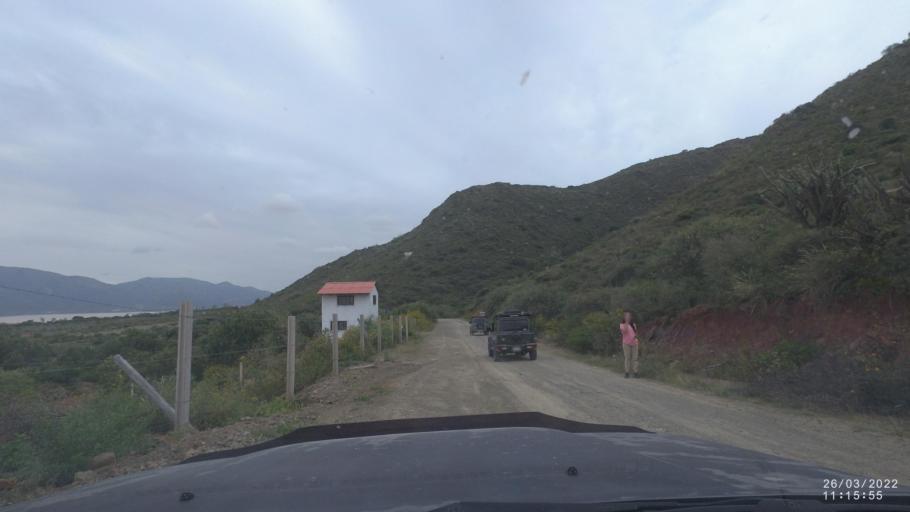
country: BO
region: Cochabamba
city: Tarata
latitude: -17.5342
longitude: -66.0212
